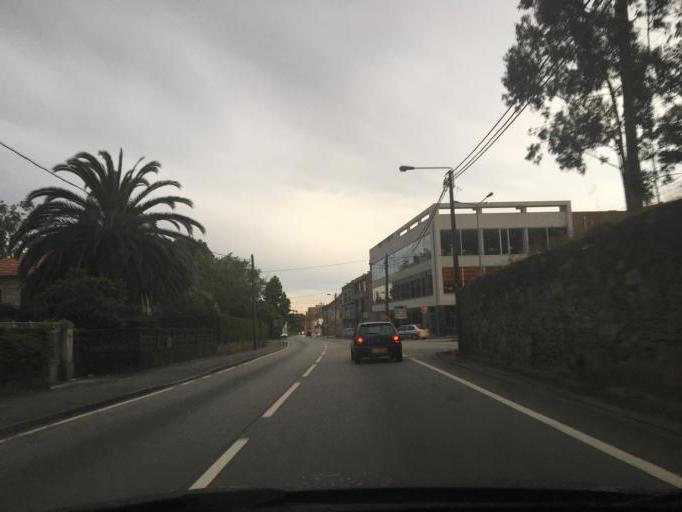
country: PT
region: Porto
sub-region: Maia
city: Anta
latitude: 41.2741
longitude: -8.6087
